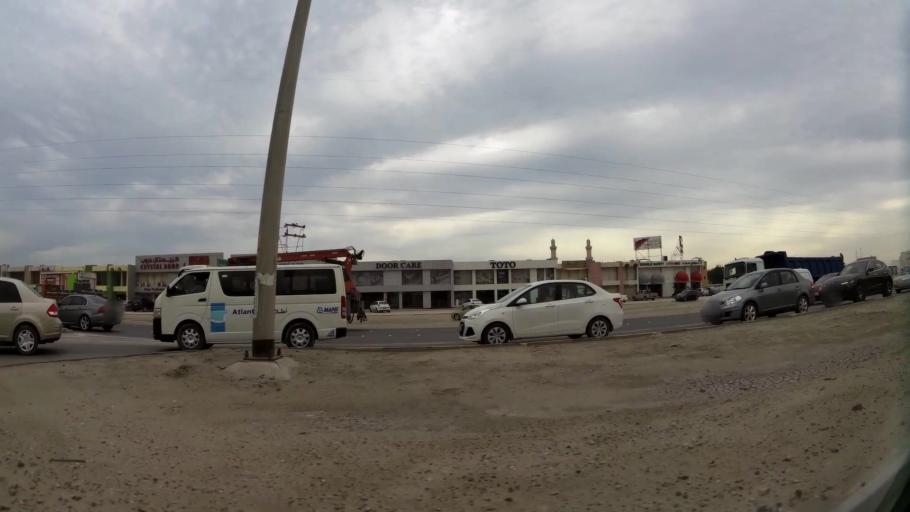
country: BH
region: Northern
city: Sitrah
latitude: 26.1618
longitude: 50.6046
